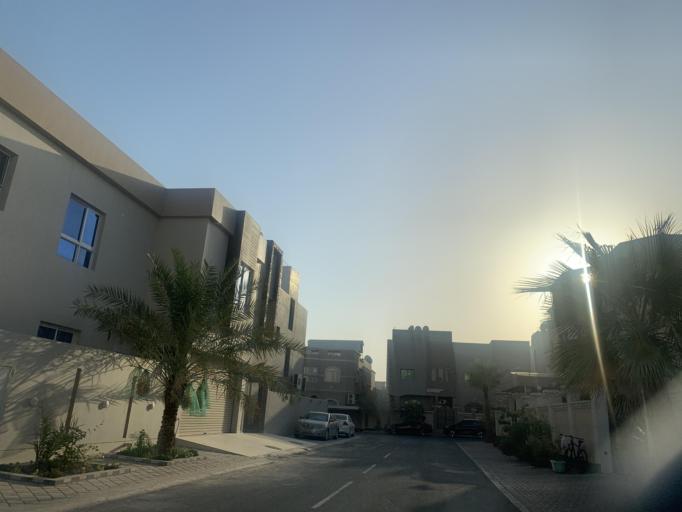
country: BH
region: Northern
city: Madinat `Isa
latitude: 26.1906
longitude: 50.4809
